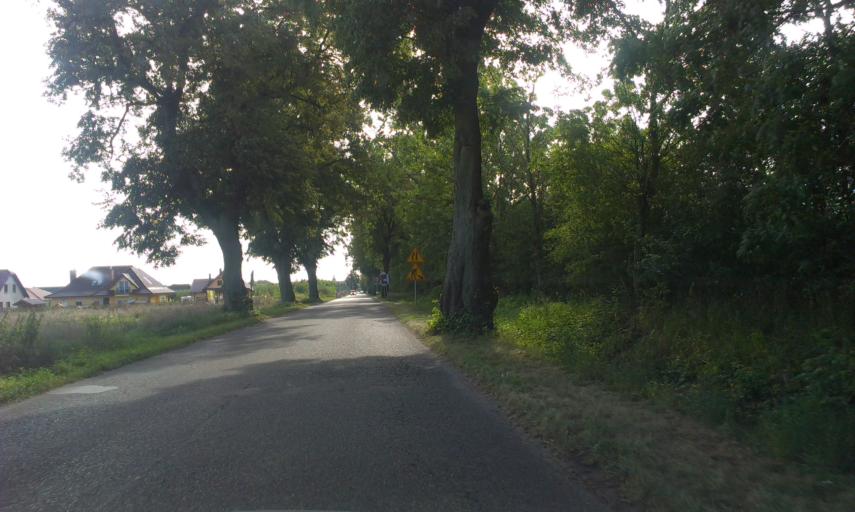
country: PL
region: Greater Poland Voivodeship
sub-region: Powiat zlotowski
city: Zlotow
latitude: 53.3780
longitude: 17.0195
